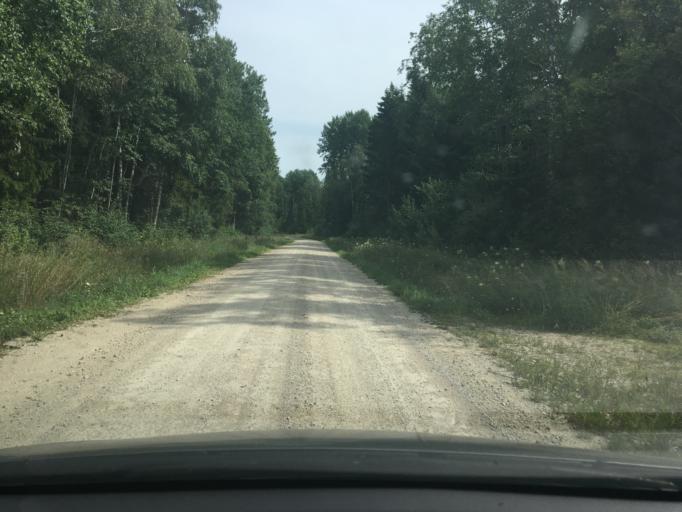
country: EE
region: Raplamaa
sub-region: Maerjamaa vald
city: Marjamaa
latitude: 58.9547
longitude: 24.5915
